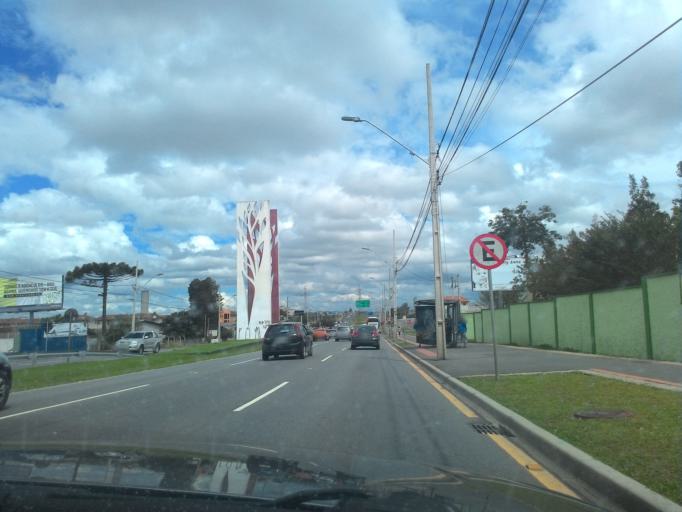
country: BR
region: Parana
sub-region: Pinhais
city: Pinhais
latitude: -25.4555
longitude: -49.2279
